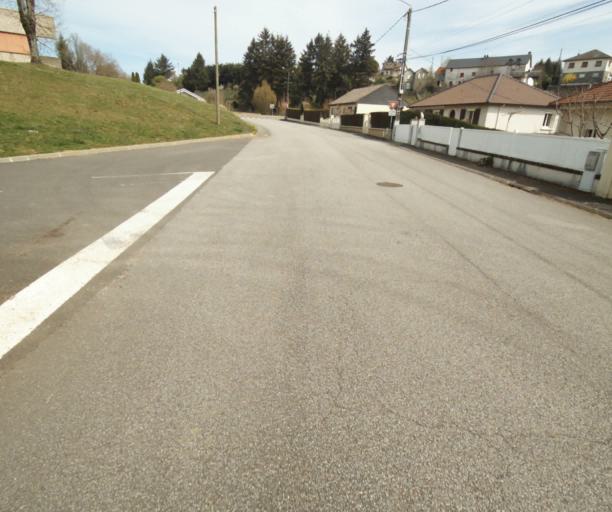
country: FR
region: Limousin
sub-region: Departement de la Correze
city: Naves
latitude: 45.3119
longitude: 1.7699
